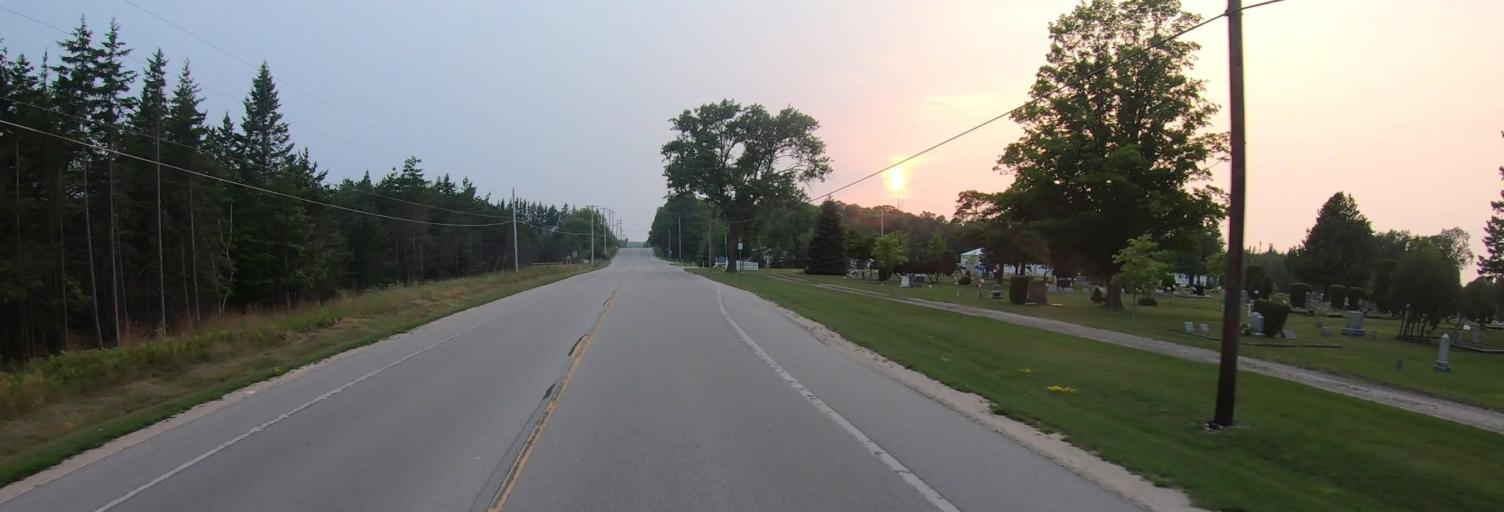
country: US
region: Michigan
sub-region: Mackinac County
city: Saint Ignace
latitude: 45.7816
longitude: -84.7553
